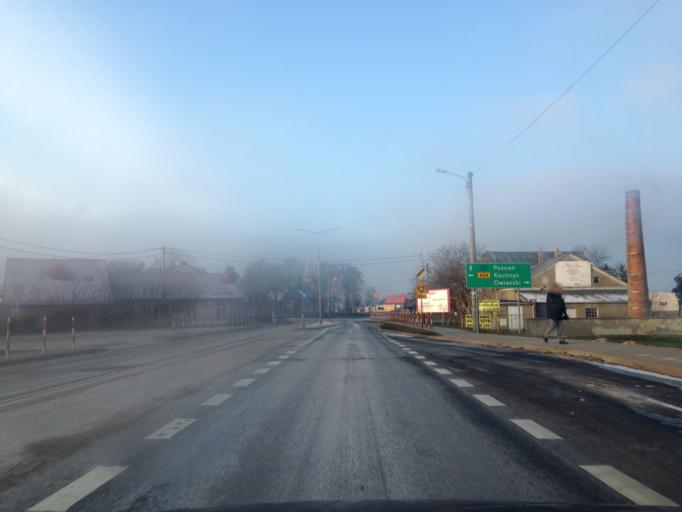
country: PL
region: Greater Poland Voivodeship
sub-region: Powiat gnieznienski
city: Lubowo
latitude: 52.5119
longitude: 17.4551
